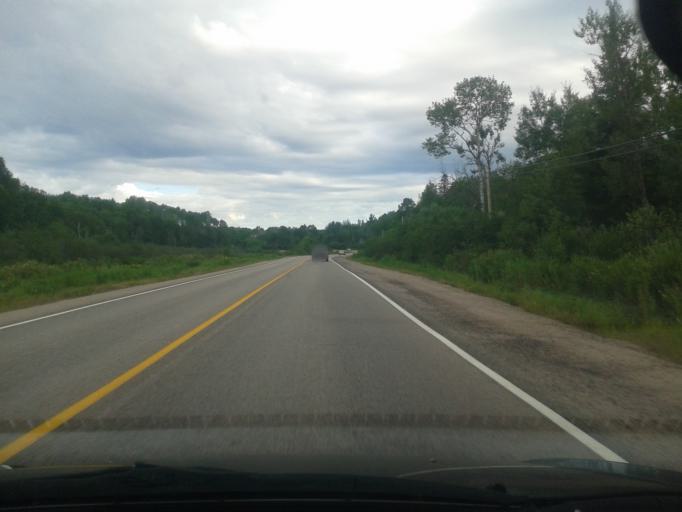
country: CA
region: Ontario
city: Powassan
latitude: 46.1925
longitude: -79.3180
